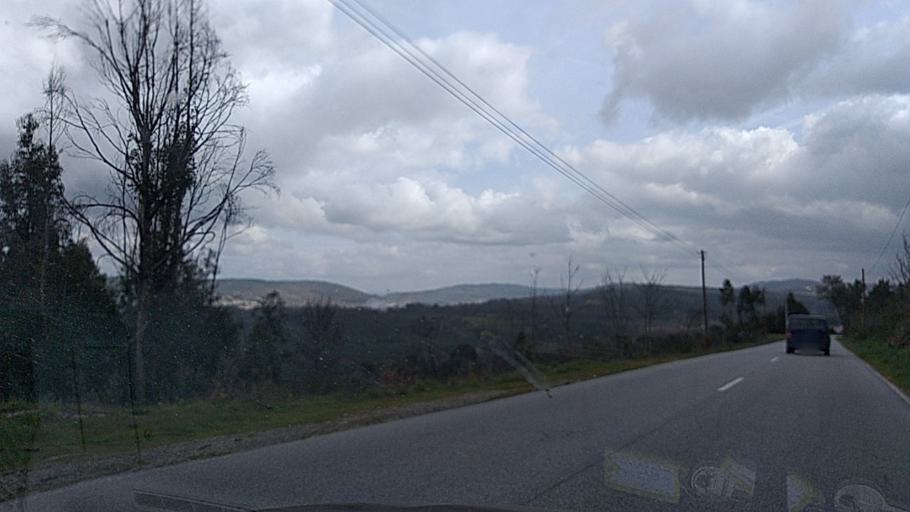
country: PT
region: Viseu
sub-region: Mangualde
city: Mangualde
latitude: 40.6107
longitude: -7.6988
